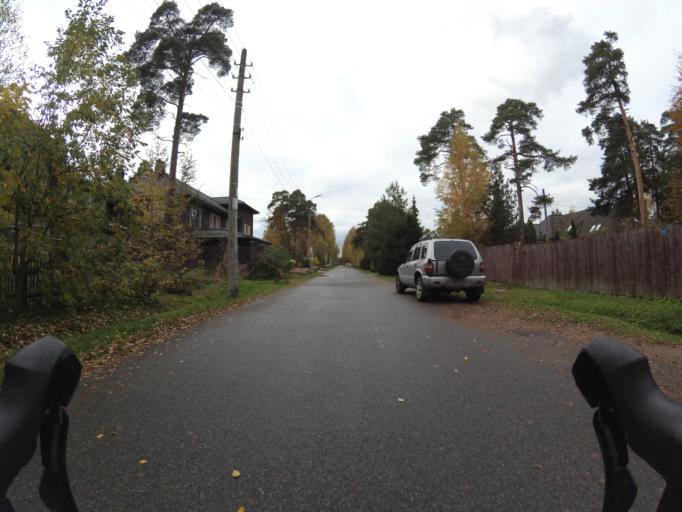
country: RU
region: St.-Petersburg
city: Lakhtinskiy
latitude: 60.0012
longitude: 30.1441
